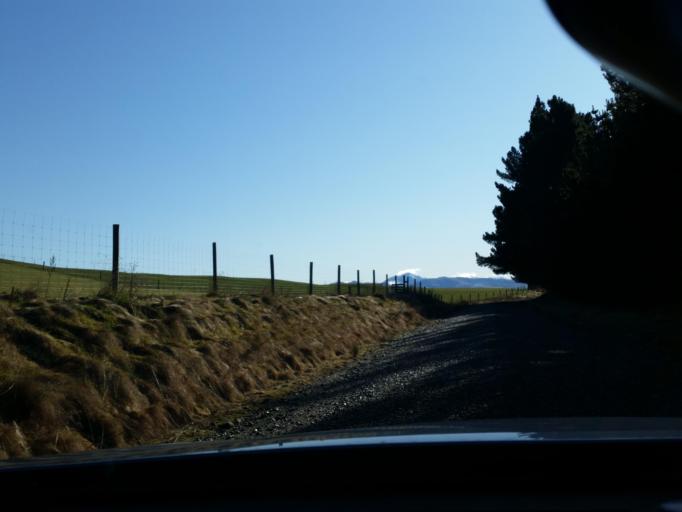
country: NZ
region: Southland
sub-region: Gore District
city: Gore
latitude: -45.8218
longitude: 168.7351
